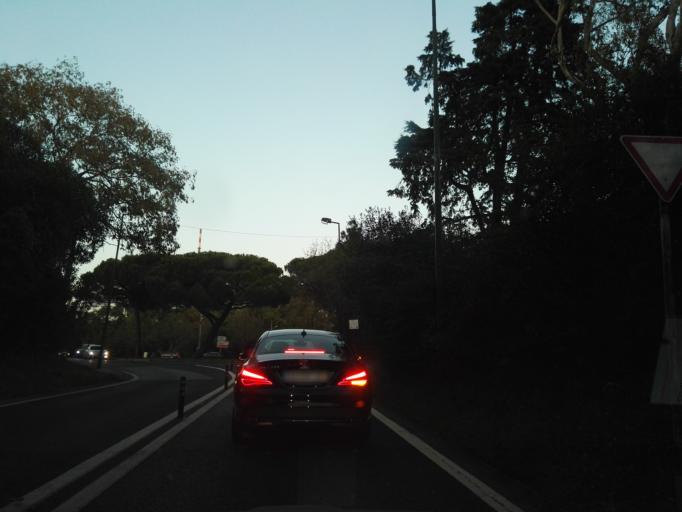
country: PT
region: Lisbon
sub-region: Oeiras
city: Alges
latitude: 38.7240
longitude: -9.1944
